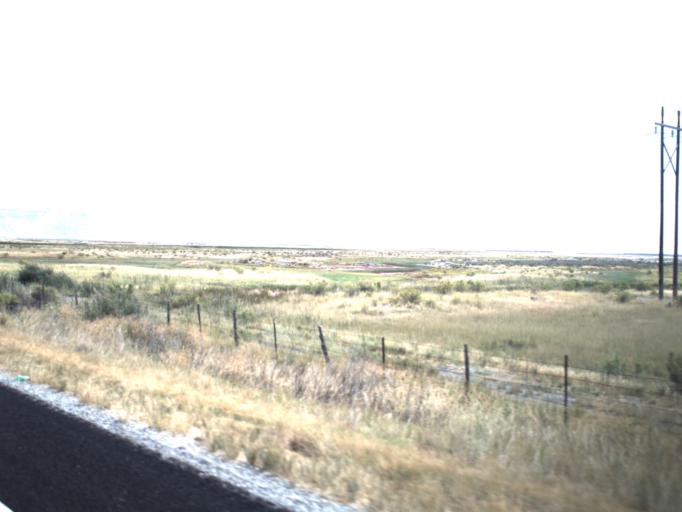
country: US
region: Utah
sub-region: Box Elder County
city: Tremonton
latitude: 41.6139
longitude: -112.3737
